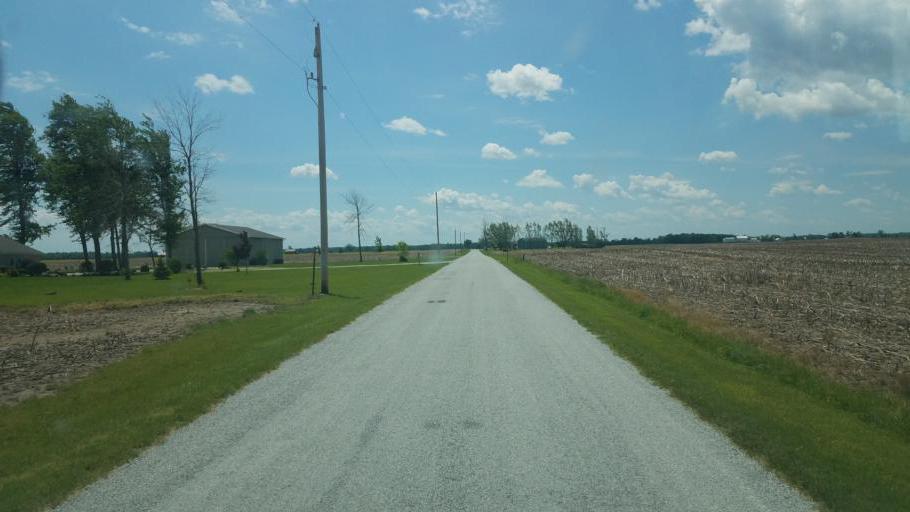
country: US
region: Ohio
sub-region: Hardin County
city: Forest
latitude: 40.6833
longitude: -83.4600
